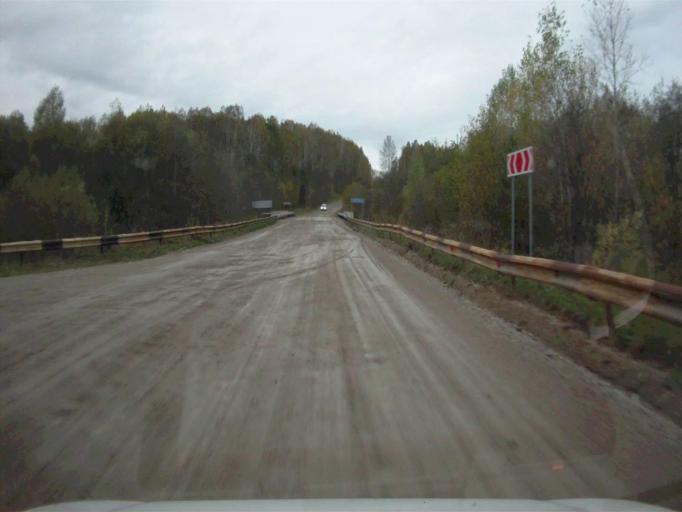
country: RU
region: Chelyabinsk
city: Nyazepetrovsk
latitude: 56.1337
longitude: 59.3127
